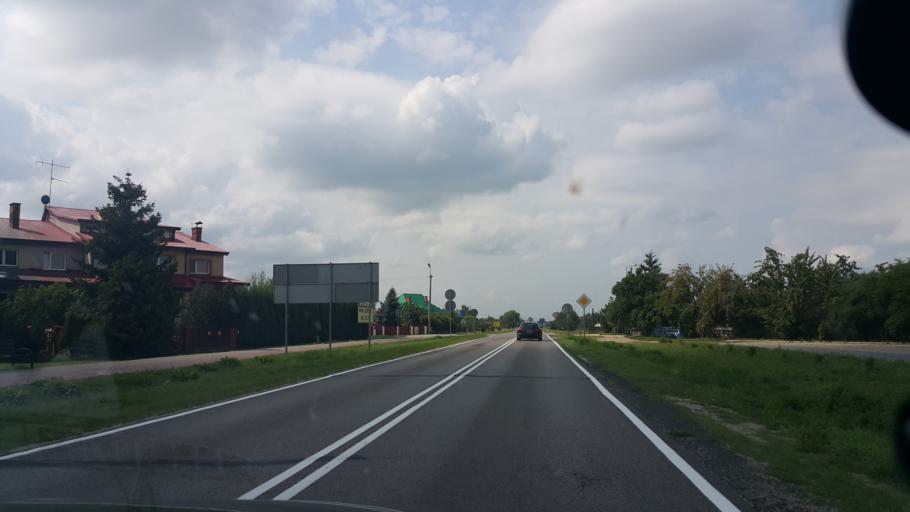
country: PL
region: Lublin Voivodeship
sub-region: Powiat wlodawski
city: Wlodawa
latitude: 51.5457
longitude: 23.5427
